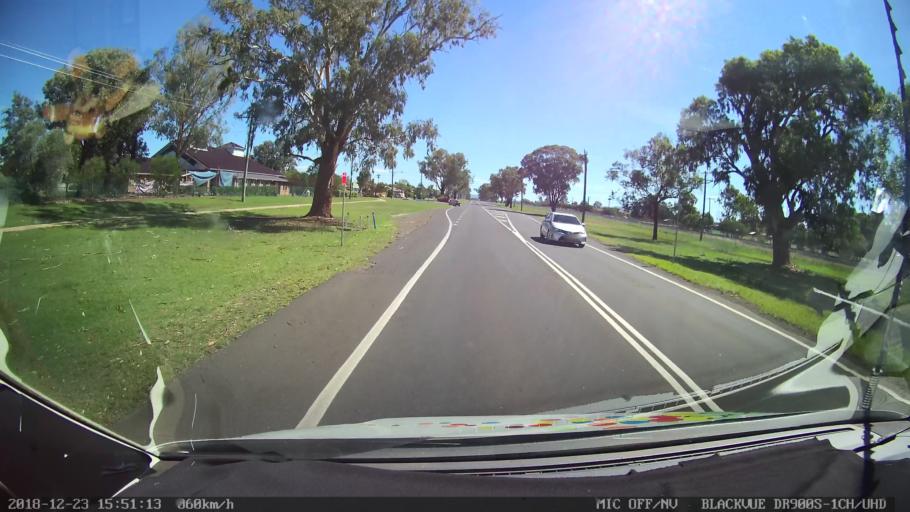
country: AU
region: New South Wales
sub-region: Tamworth Municipality
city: South Tamworth
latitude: -31.1110
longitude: 150.8972
